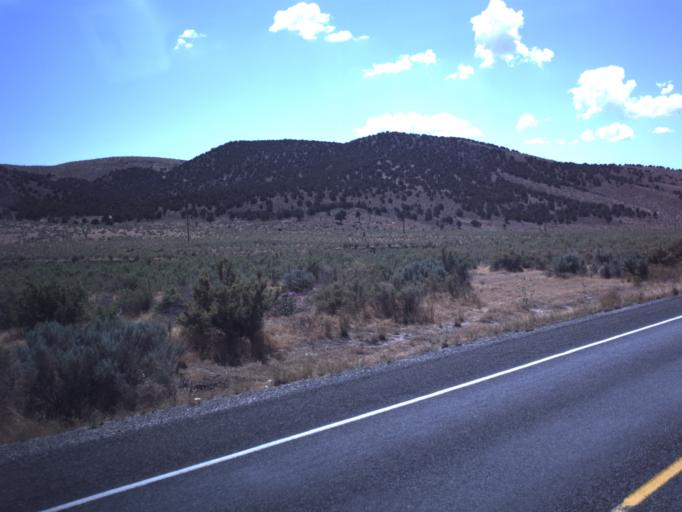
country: US
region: Utah
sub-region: Juab County
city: Nephi
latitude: 39.6237
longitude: -112.1236
